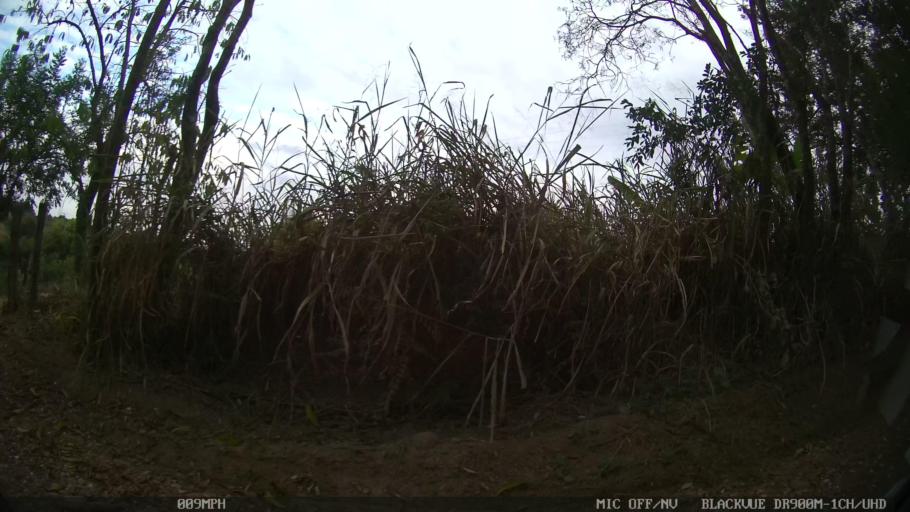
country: BR
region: Sao Paulo
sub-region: Americana
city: Americana
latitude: -22.6583
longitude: -47.3689
